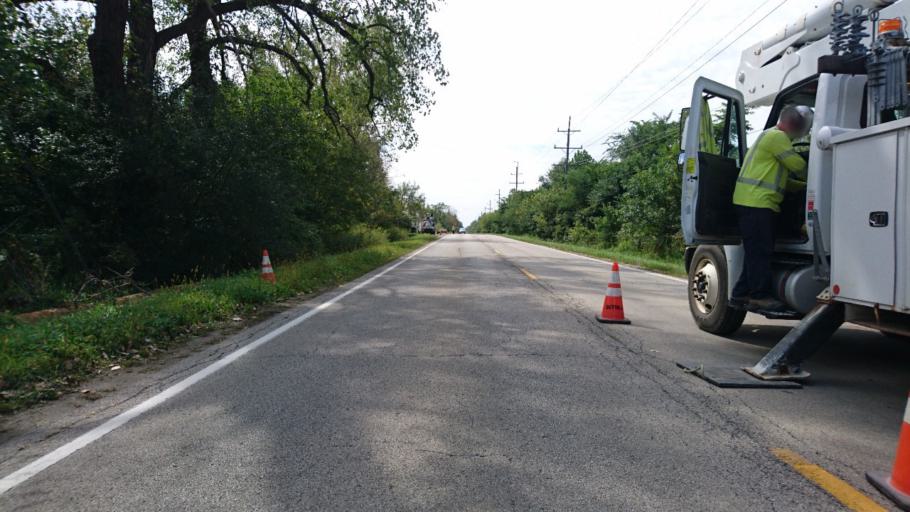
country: US
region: Illinois
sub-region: Will County
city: Braidwood
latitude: 41.2858
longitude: -88.1841
